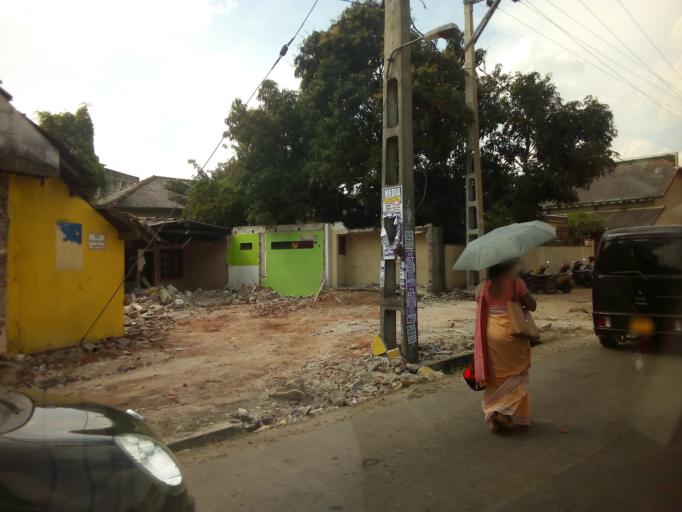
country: LK
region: North Western
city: Kurunegala
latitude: 7.4888
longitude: 80.3653
